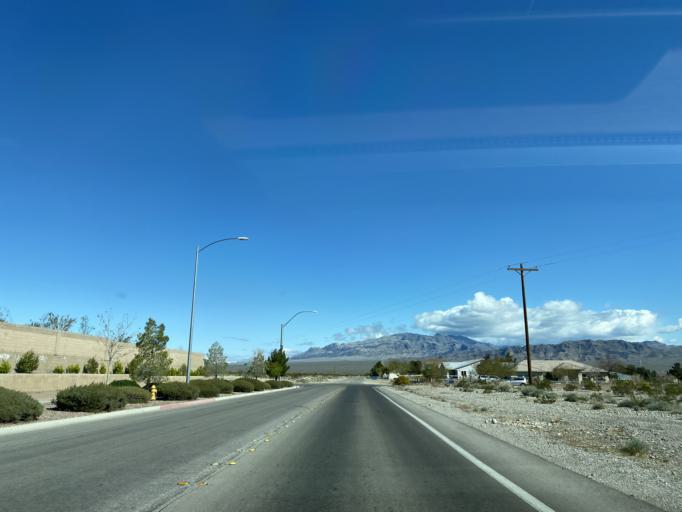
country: US
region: Nevada
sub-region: Clark County
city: North Las Vegas
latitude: 36.3276
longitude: -115.2876
